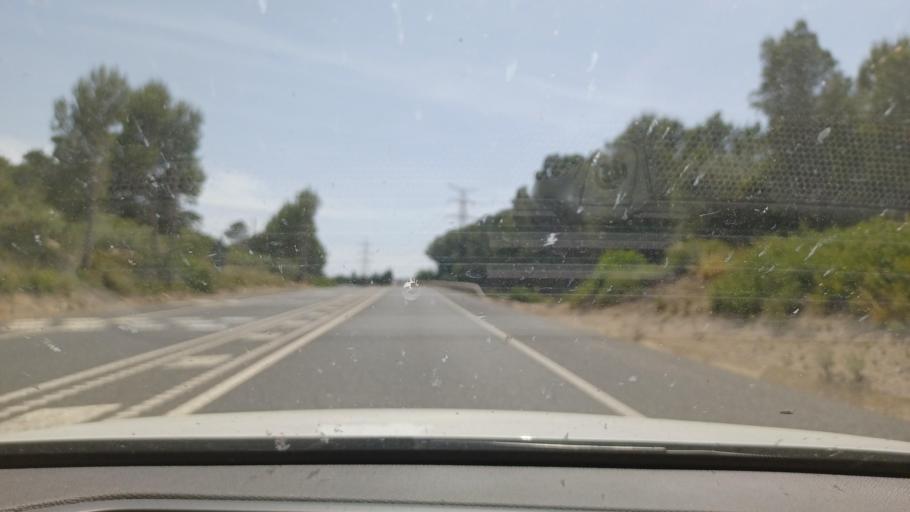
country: ES
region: Catalonia
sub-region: Provincia de Tarragona
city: l'Ametlla de Mar
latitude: 40.9751
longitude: 0.8834
